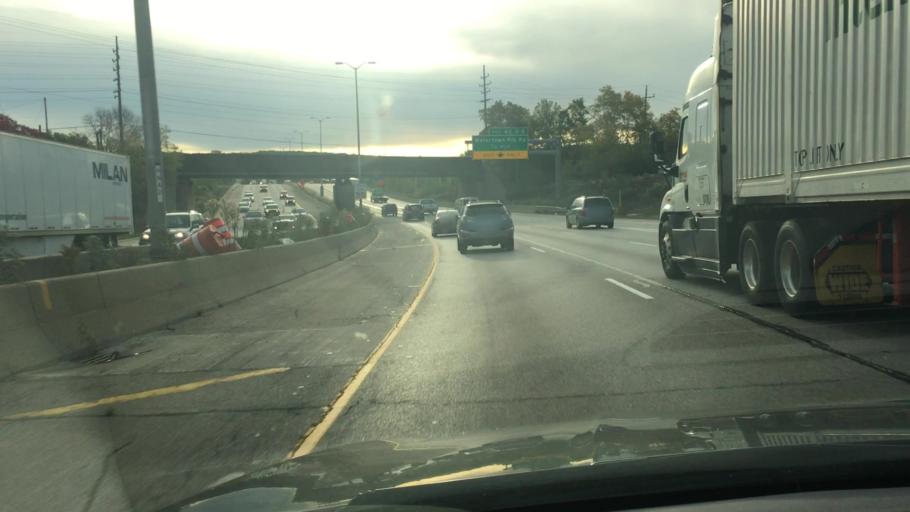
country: US
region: Wisconsin
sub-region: Waukesha County
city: Elm Grove
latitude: 43.0568
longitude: -88.0512
